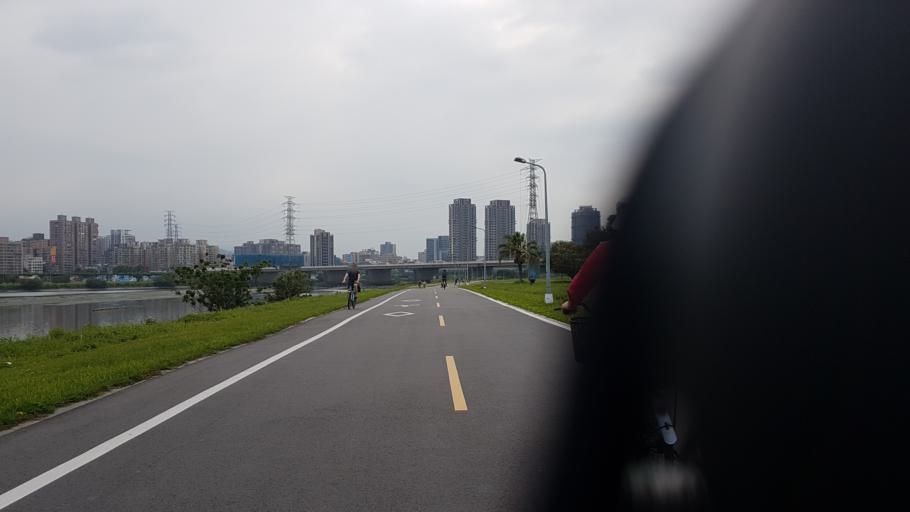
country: TW
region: Taipei
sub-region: Taipei
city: Banqiao
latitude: 25.0138
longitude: 121.4992
